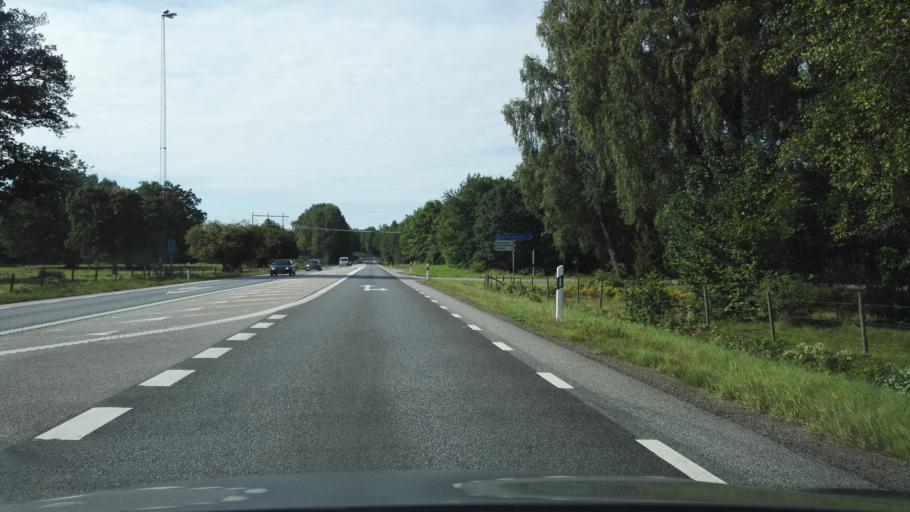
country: SE
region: Kronoberg
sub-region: Vaxjo Kommun
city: Vaexjoe
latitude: 56.8672
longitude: 14.7373
